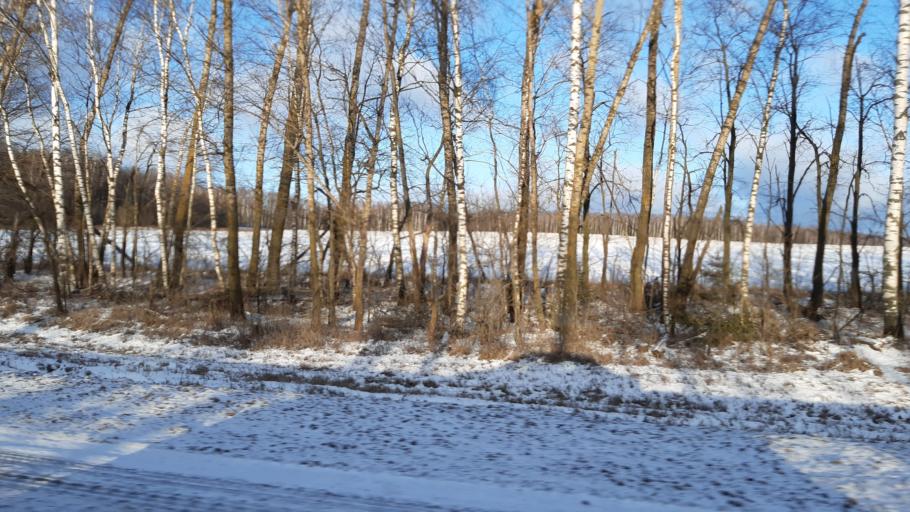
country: RU
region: Vladimir
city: Arsaki
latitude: 56.2903
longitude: 38.3838
